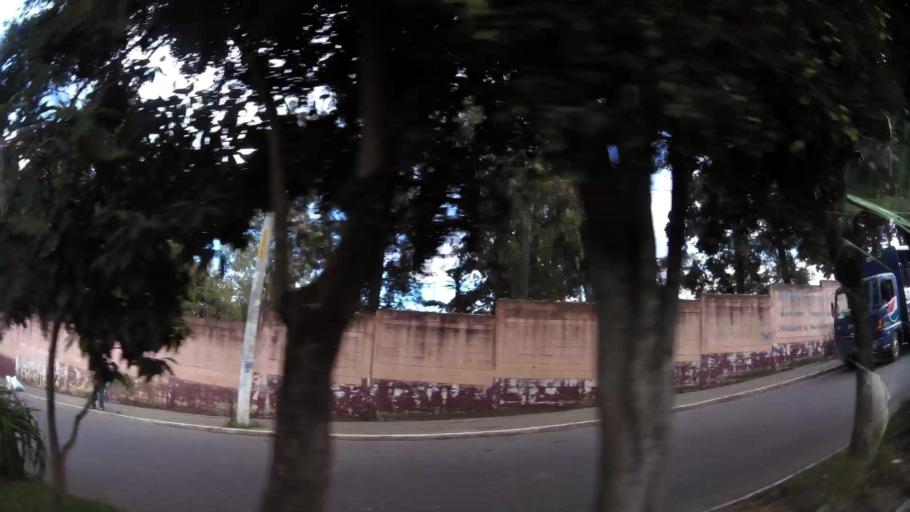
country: GT
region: Guatemala
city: Mixco
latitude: 14.6702
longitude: -90.5677
